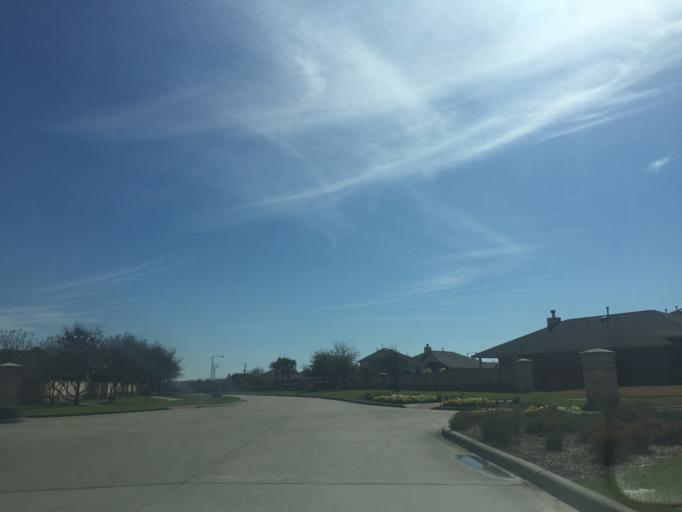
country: US
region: Texas
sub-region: Galveston County
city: Bacliff
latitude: 29.5120
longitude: -95.0189
